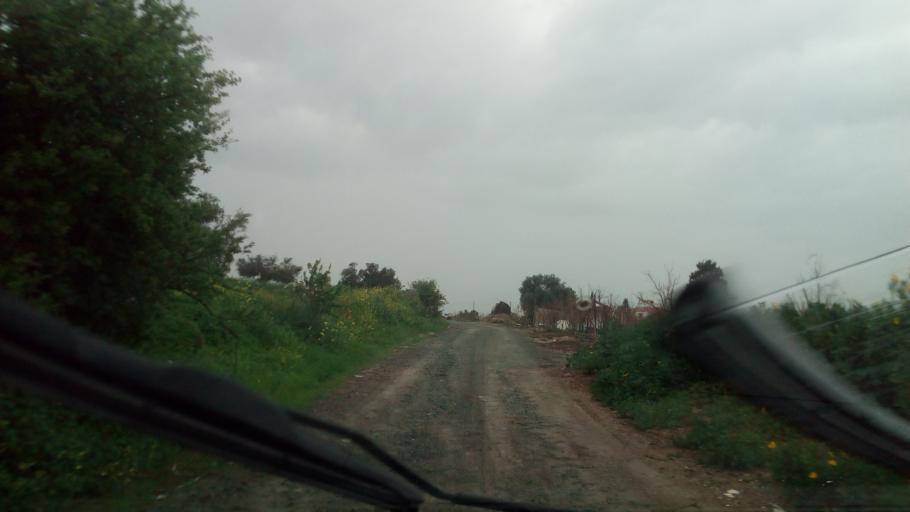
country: CY
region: Larnaka
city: Kofinou
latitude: 34.8517
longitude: 33.4667
